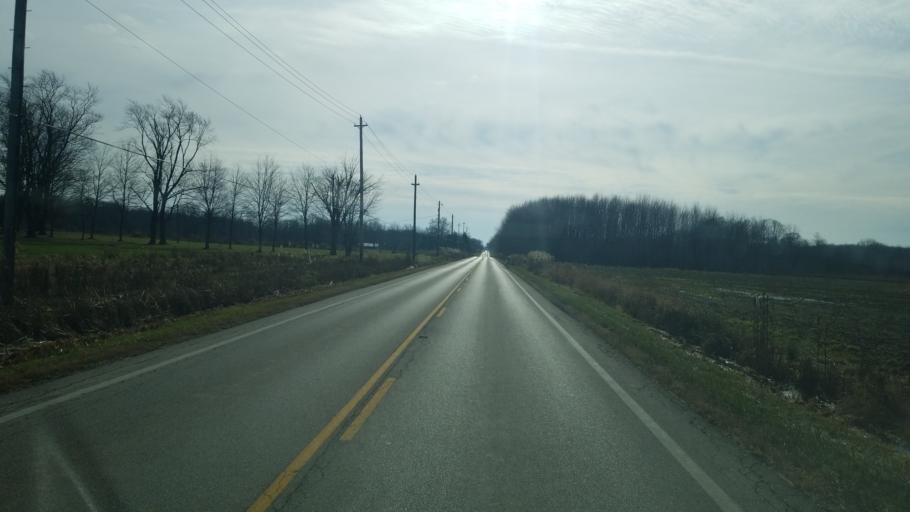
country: US
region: Ohio
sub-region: Ashtabula County
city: Geneva
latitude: 41.7148
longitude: -80.9526
